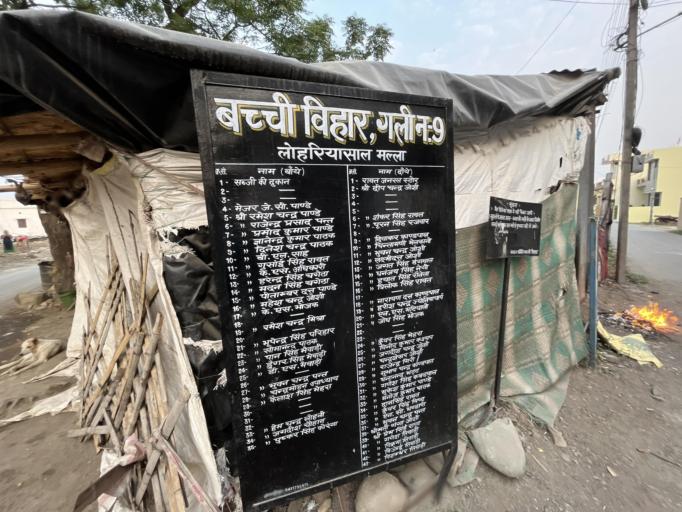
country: IN
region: Uttarakhand
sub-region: Naini Tal
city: Haldwani
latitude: 29.2278
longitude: 79.5019
